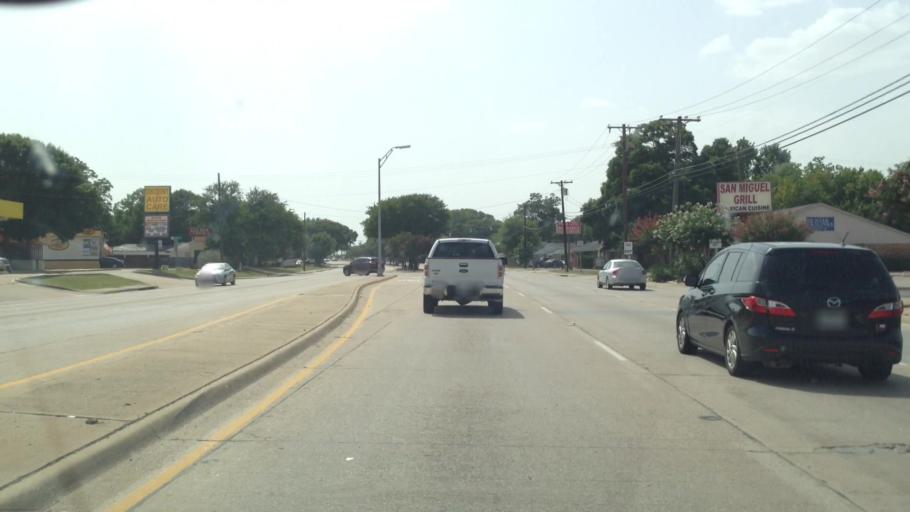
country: US
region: Texas
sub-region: Collin County
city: McKinney
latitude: 33.2154
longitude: -96.6205
